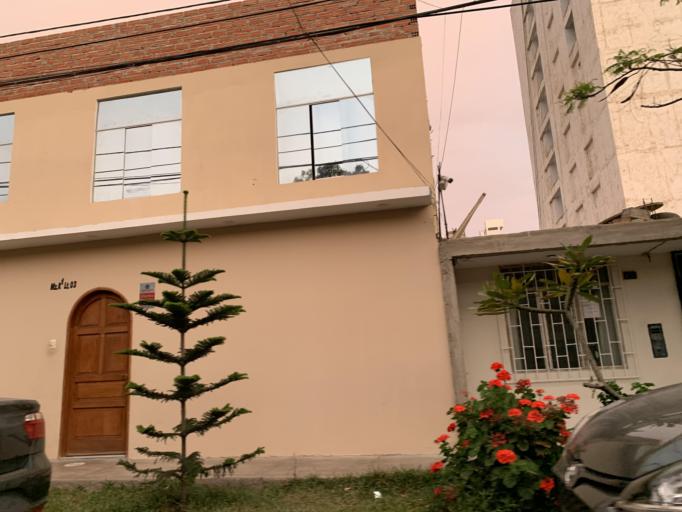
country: PE
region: La Libertad
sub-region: Provincia de Trujillo
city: Trujillo
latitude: -8.1085
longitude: -79.0452
